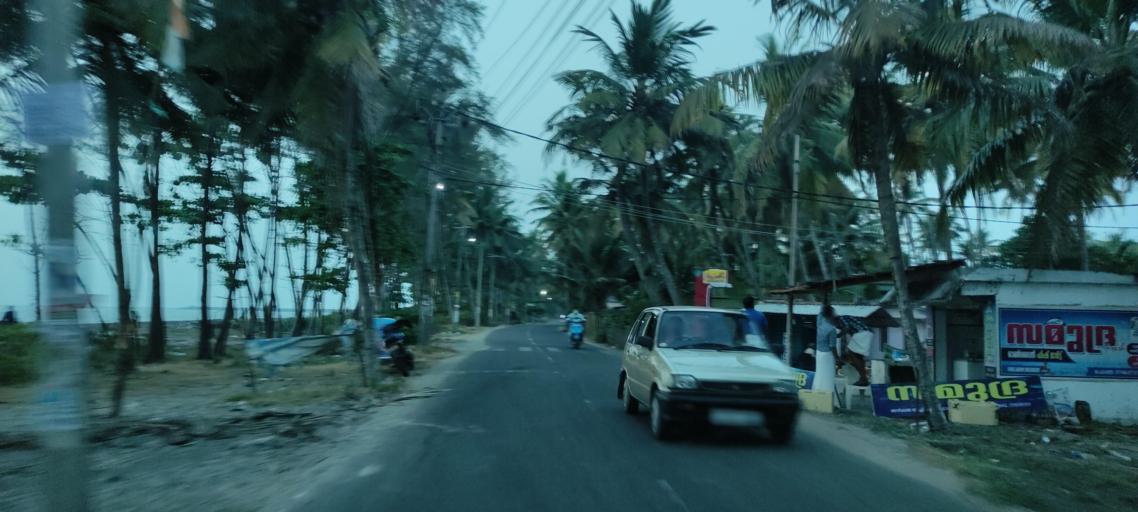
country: IN
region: Kerala
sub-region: Alappuzha
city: Kayankulam
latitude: 9.1272
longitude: 76.4672
